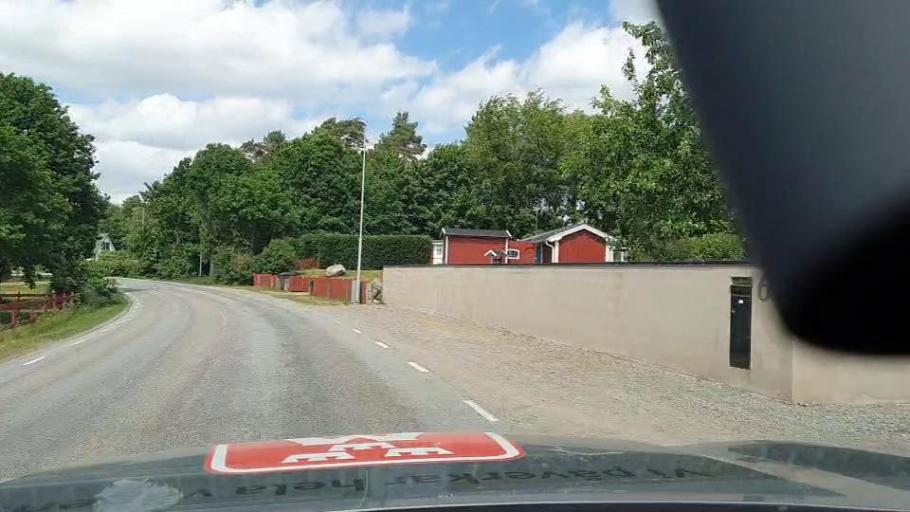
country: SE
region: Blekinge
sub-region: Karlshamns Kommun
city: Morrum
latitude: 56.1099
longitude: 14.6851
